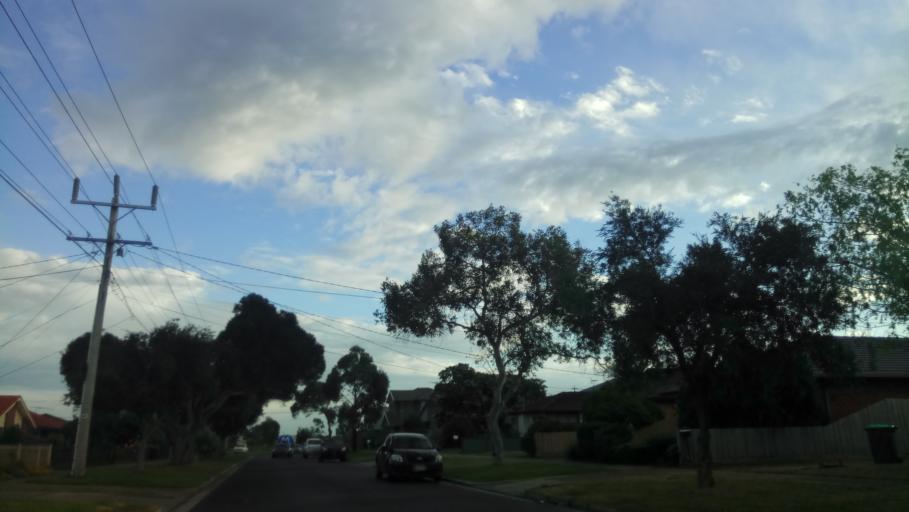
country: AU
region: Victoria
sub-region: Hobsons Bay
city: Altona Meadows
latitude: -37.8673
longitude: 144.7860
